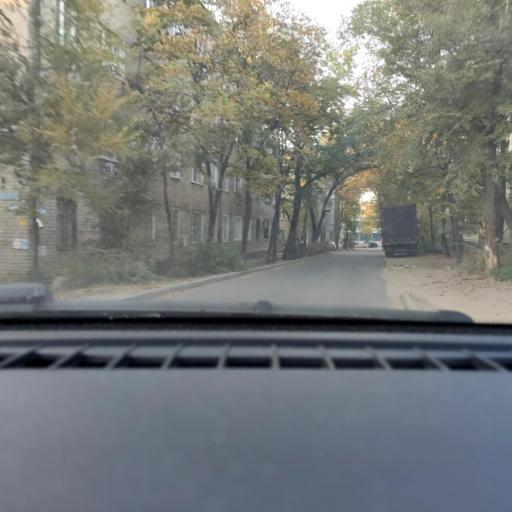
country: RU
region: Voronezj
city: Maslovka
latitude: 51.6159
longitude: 39.2413
